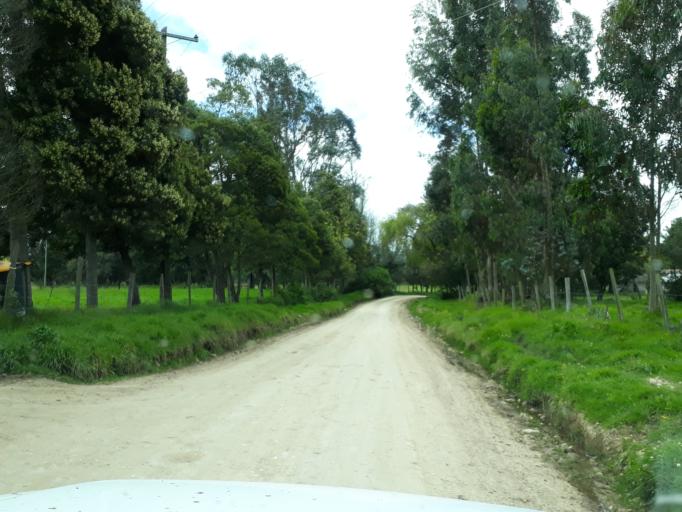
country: CO
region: Cundinamarca
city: Guasca
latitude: 4.8569
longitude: -73.8940
